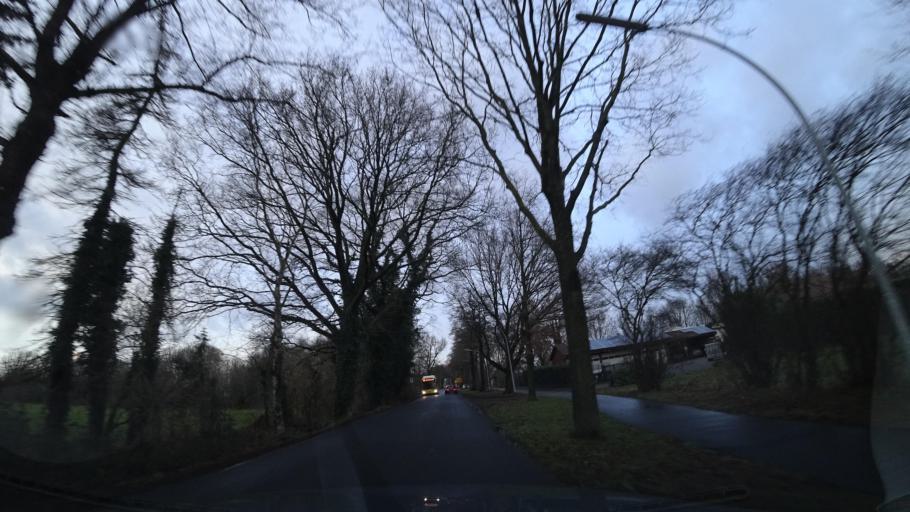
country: DE
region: Lower Saxony
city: Oldenburg
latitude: 53.1031
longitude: 8.2761
